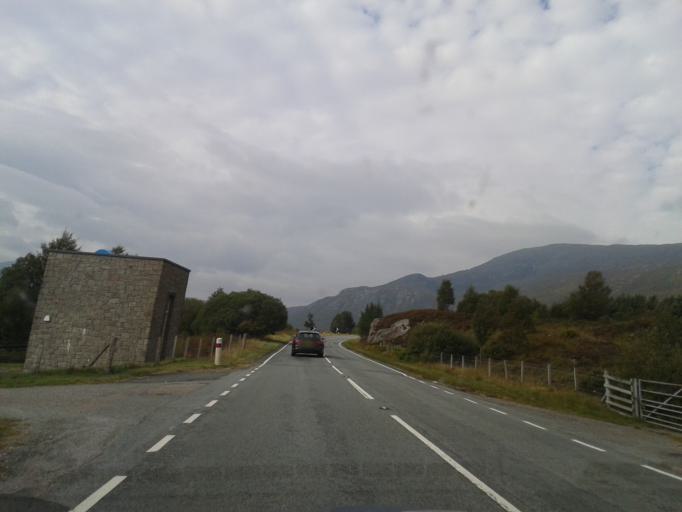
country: GB
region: Scotland
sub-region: Highland
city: Spean Bridge
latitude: 57.1469
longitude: -5.0034
